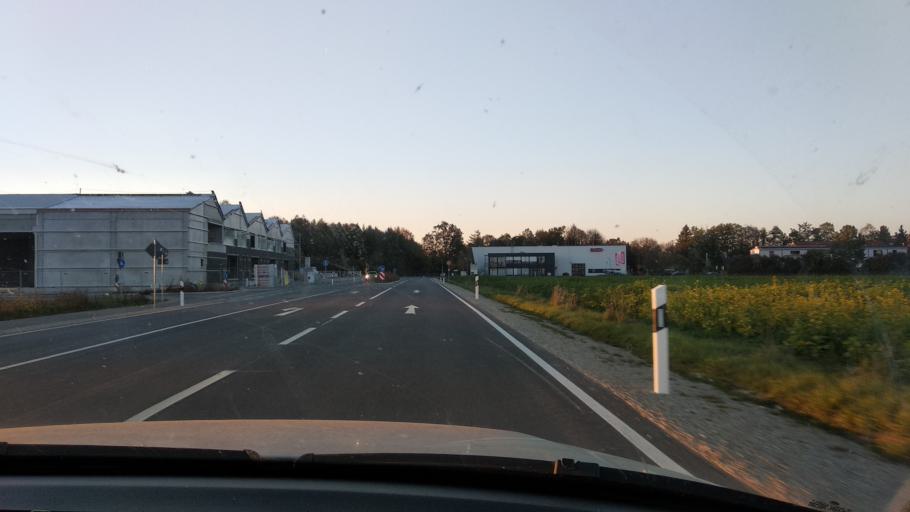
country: DE
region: Bavaria
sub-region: Upper Bavaria
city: Hohenkirchen-Siegertsbrunn
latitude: 48.0325
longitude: 11.7179
